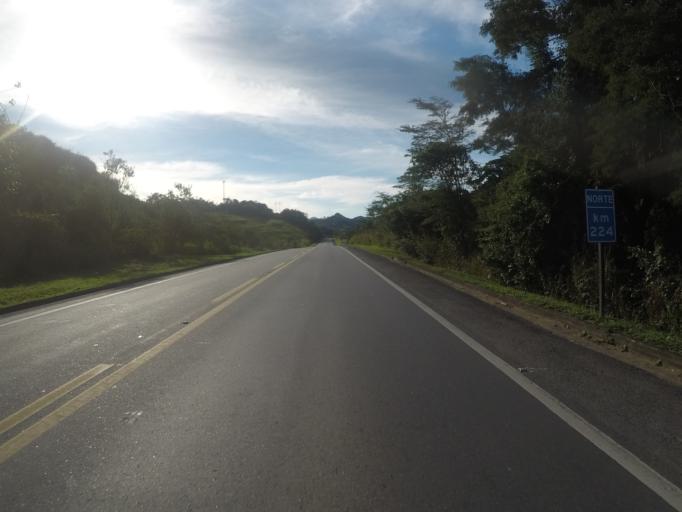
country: BR
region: Espirito Santo
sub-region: Fundao
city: Fundao
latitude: -19.8854
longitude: -40.4152
